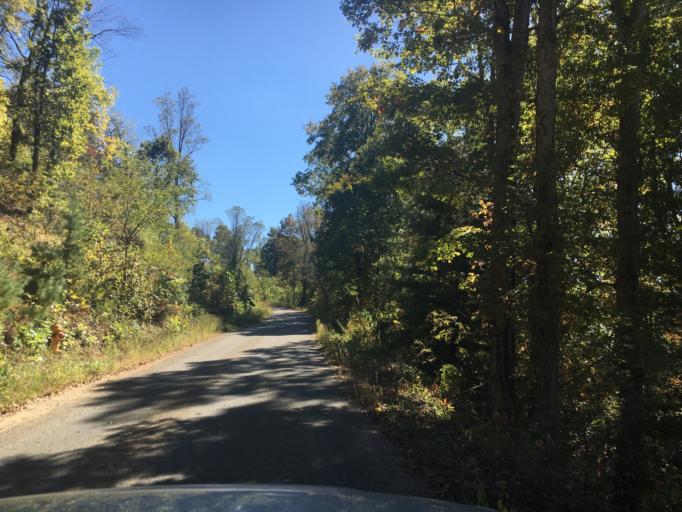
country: US
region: North Carolina
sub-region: Buncombe County
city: Woodfin
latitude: 35.6475
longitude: -82.5891
